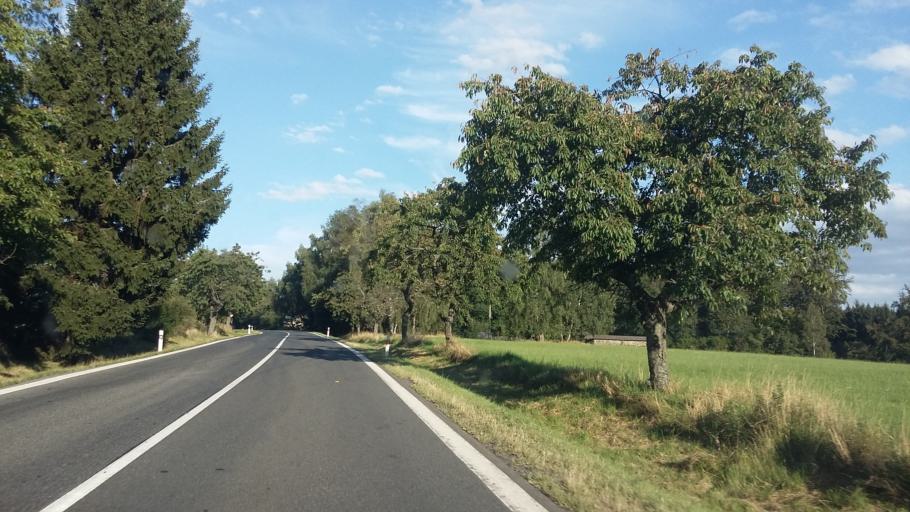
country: CZ
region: Plzensky
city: Strasice
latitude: 49.6229
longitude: 13.7514
